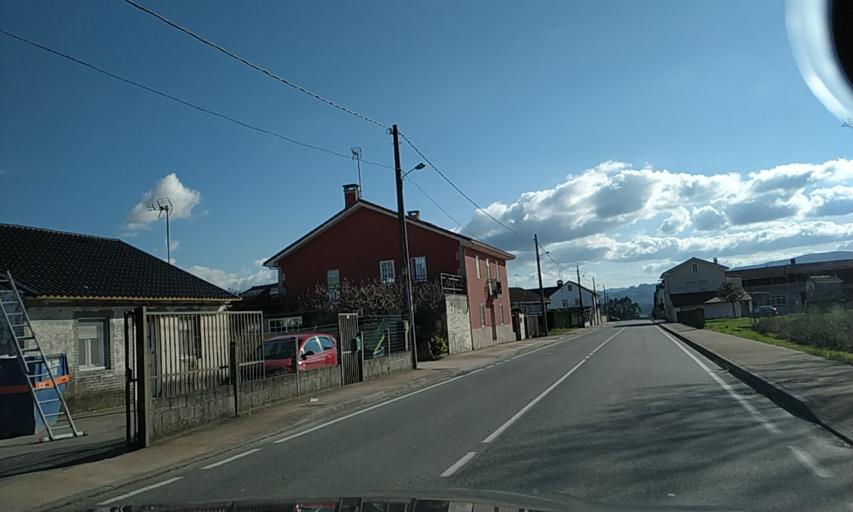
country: ES
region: Galicia
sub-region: Provincia da Coruna
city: Ribeira
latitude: 42.7123
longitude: -8.4463
